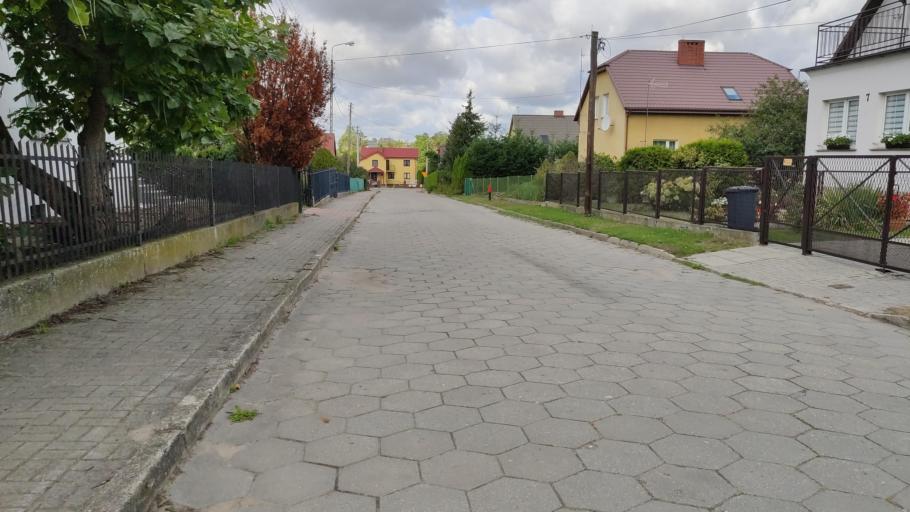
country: PL
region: Kujawsko-Pomorskie
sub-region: Powiat zninski
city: Znin
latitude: 52.8491
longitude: 17.7526
